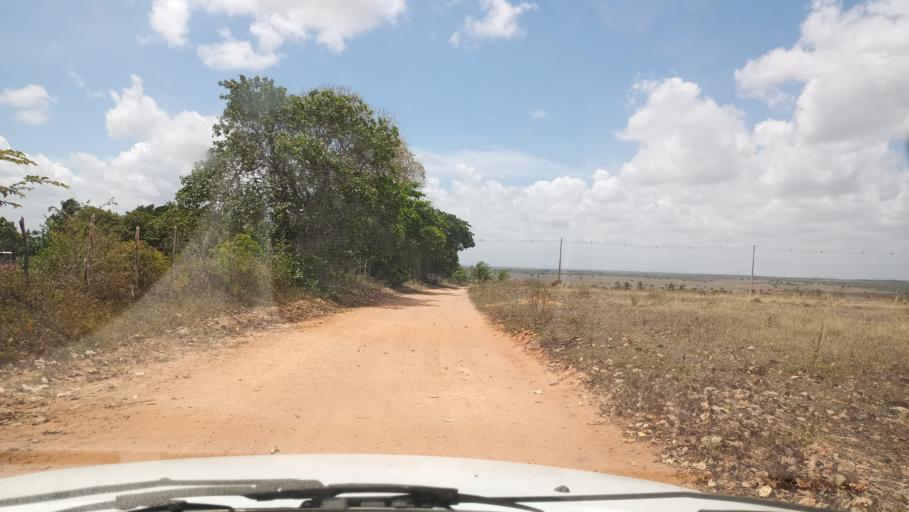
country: BR
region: Rio Grande do Norte
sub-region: Goianinha
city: Goianinha
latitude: -6.2845
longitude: -35.2873
